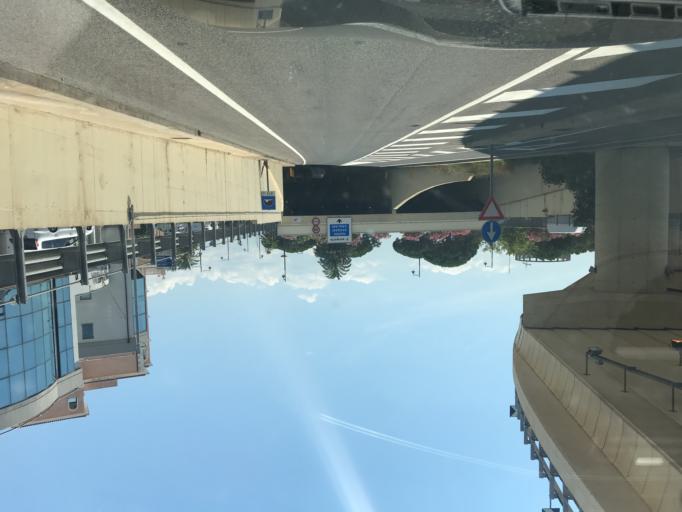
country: IT
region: Sardinia
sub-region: Provincia di Olbia-Tempio
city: Olbia
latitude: 40.9259
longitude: 9.5071
